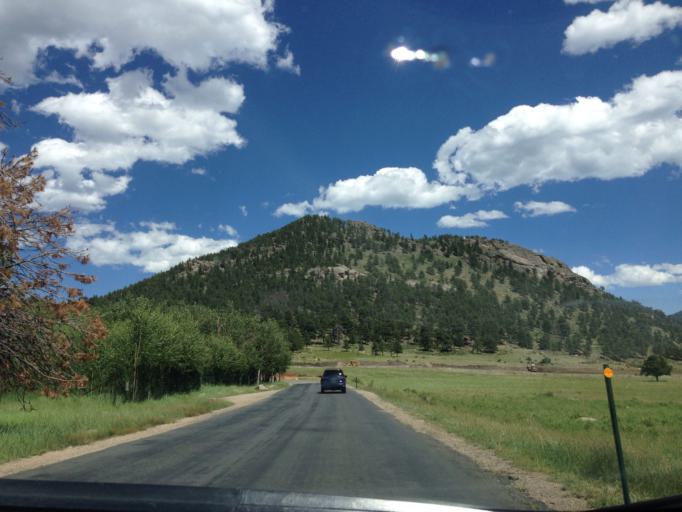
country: US
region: Colorado
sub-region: Larimer County
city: Estes Park
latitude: 40.3579
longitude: -105.5889
